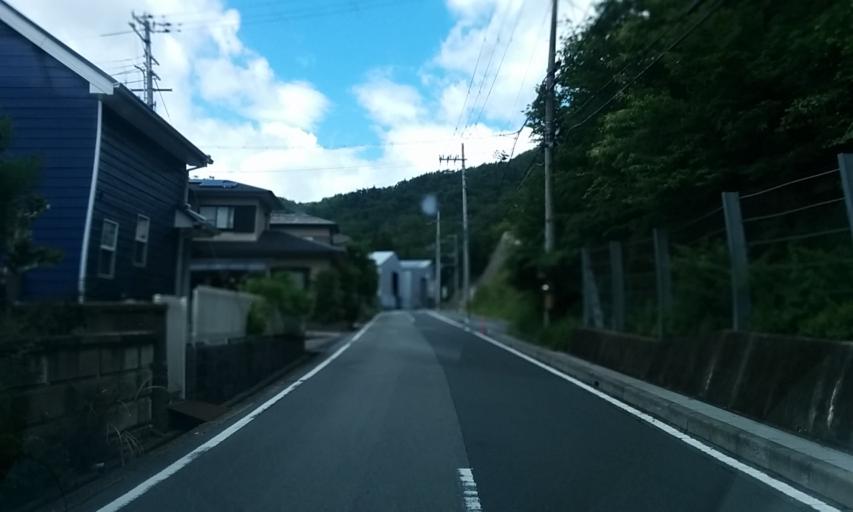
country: JP
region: Kyoto
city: Kameoka
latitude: 35.0157
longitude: 135.4235
